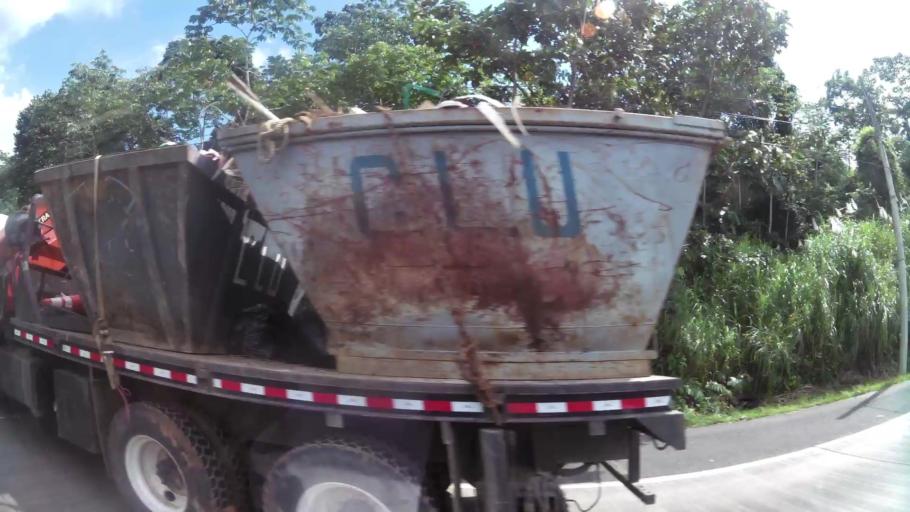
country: PA
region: Panama
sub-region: Distrito de Panama
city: Paraiso
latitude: 9.0401
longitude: -79.5702
